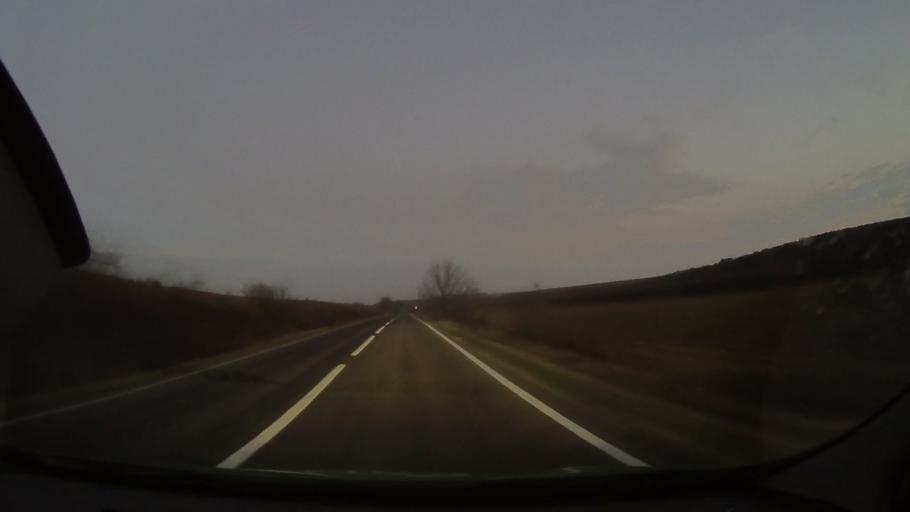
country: RO
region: Constanta
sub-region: Comuna Ion Corvin
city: Ion Corvin
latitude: 44.1052
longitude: 27.7822
